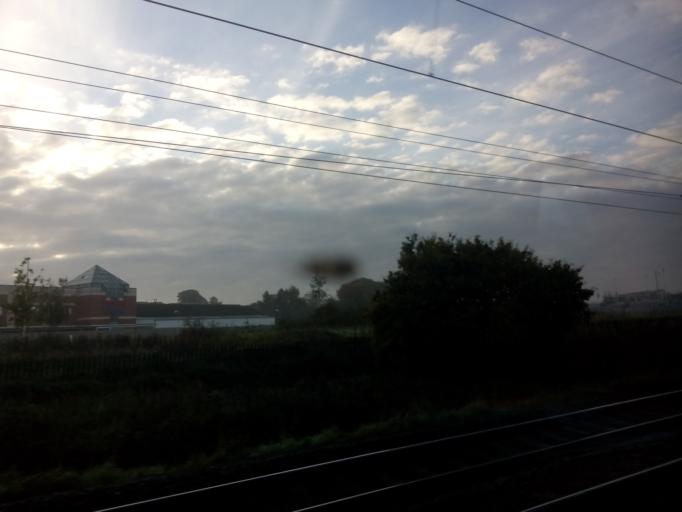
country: GB
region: England
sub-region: City of York
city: Bishopthorpe
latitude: 53.9319
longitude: -1.1176
